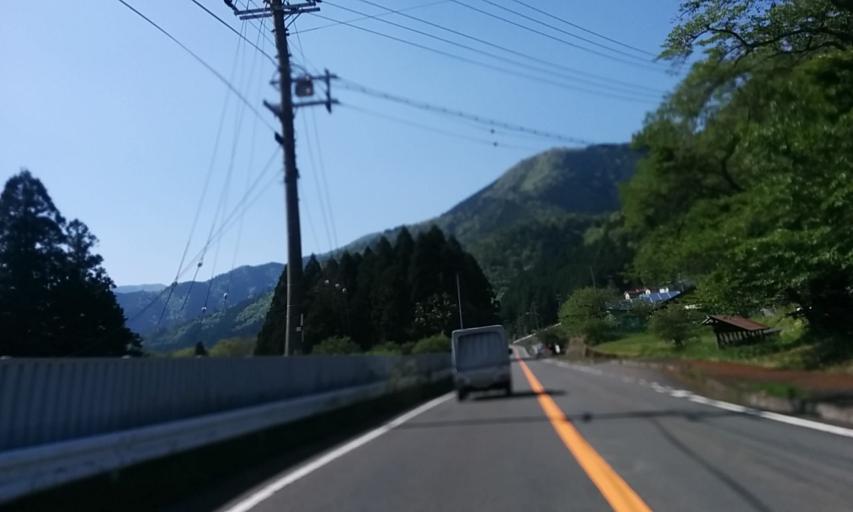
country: JP
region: Kyoto
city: Maizuru
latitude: 35.2767
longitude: 135.5434
